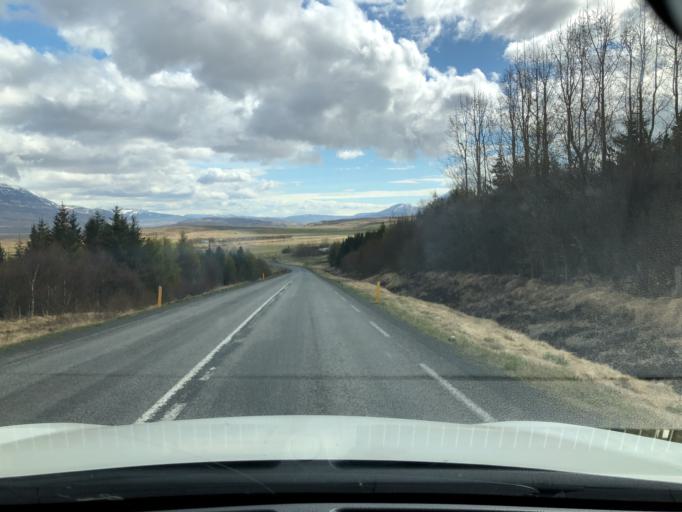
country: IS
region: Northwest
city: Saudarkrokur
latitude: 65.5478
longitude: -19.4767
